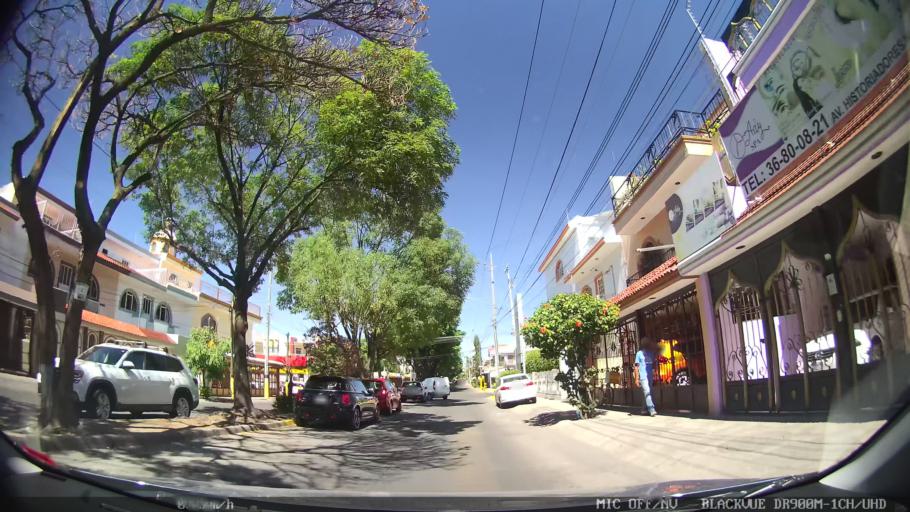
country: MX
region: Jalisco
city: Tlaquepaque
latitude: 20.6473
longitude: -103.2892
